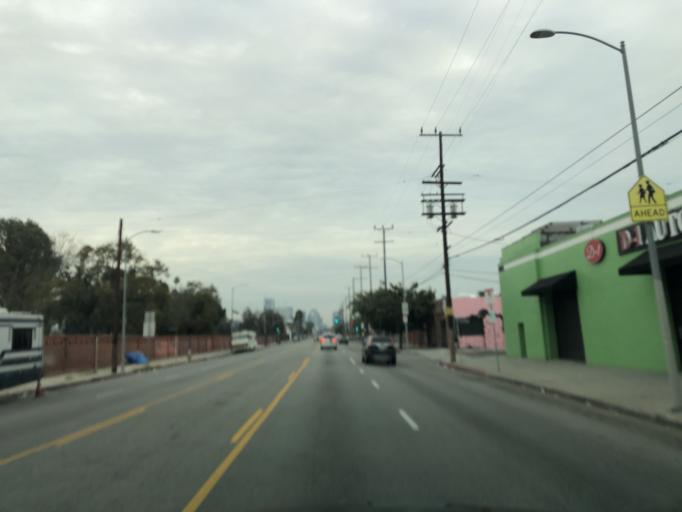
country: US
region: California
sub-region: Los Angeles County
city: Echo Park
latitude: 34.0400
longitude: -118.2981
